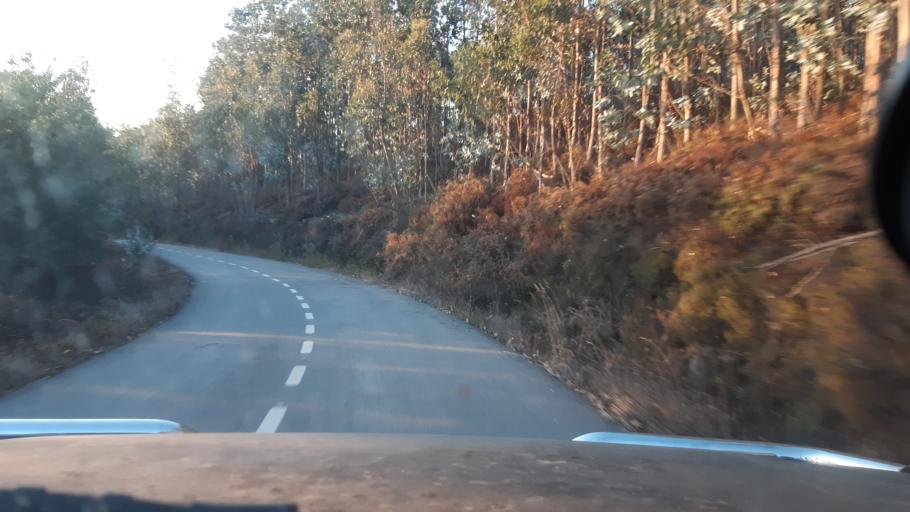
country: PT
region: Aveiro
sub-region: Agueda
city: Aguada de Cima
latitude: 40.5627
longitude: -8.3091
